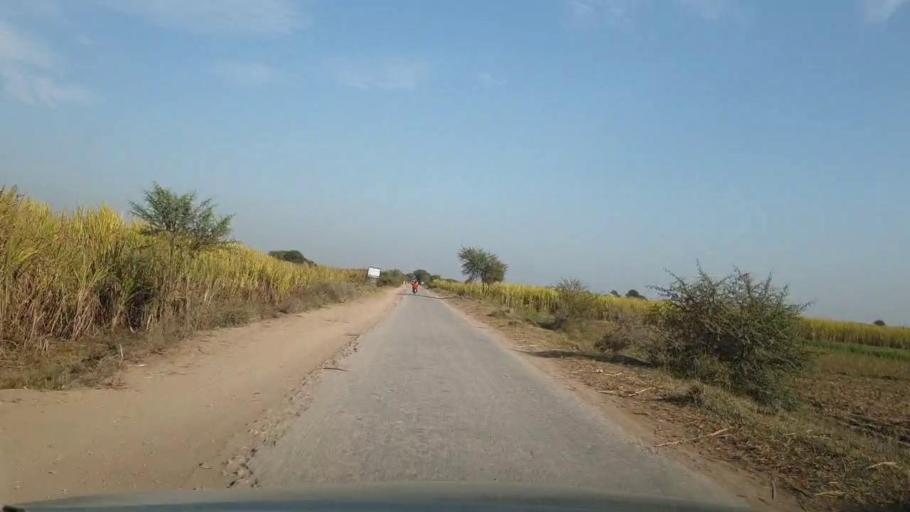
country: PK
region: Sindh
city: Tando Allahyar
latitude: 25.5936
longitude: 68.6813
